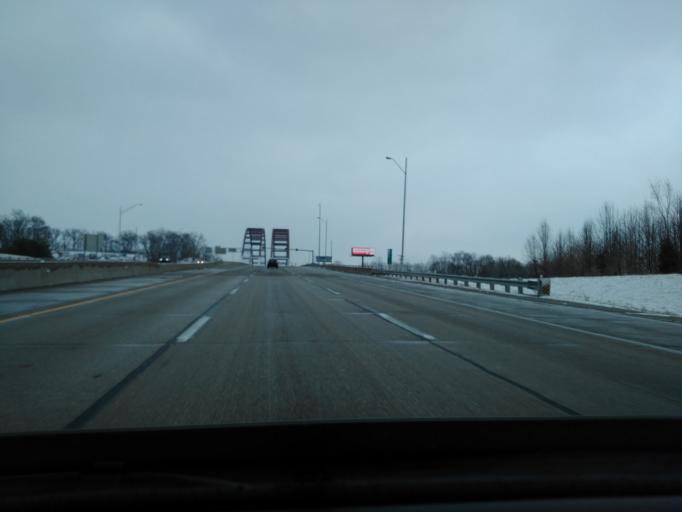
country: US
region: Missouri
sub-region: Saint Louis County
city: Oakville
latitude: 38.4894
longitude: -90.2853
